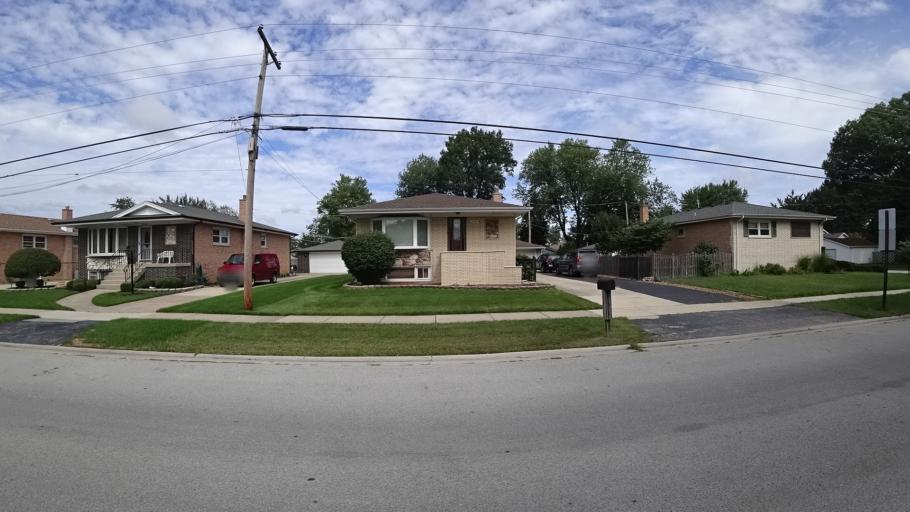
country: US
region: Illinois
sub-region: Cook County
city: Burbank
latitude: 41.7231
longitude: -87.7818
